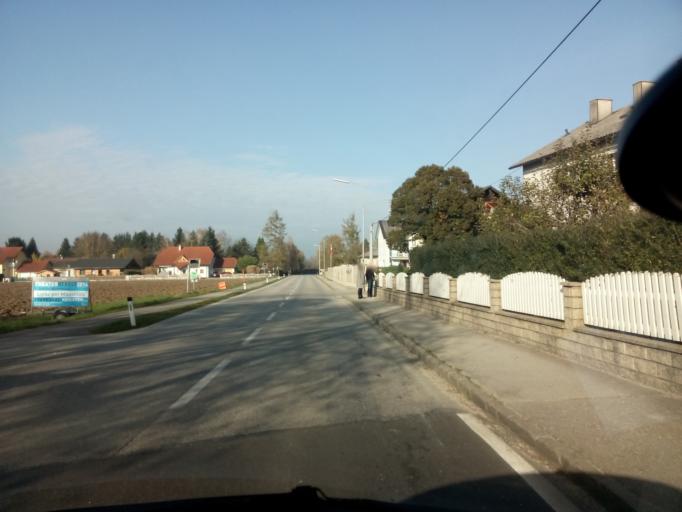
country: AT
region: Upper Austria
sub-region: Politischer Bezirk Steyr-Land
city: Bad Hall
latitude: 48.0727
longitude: 14.1903
